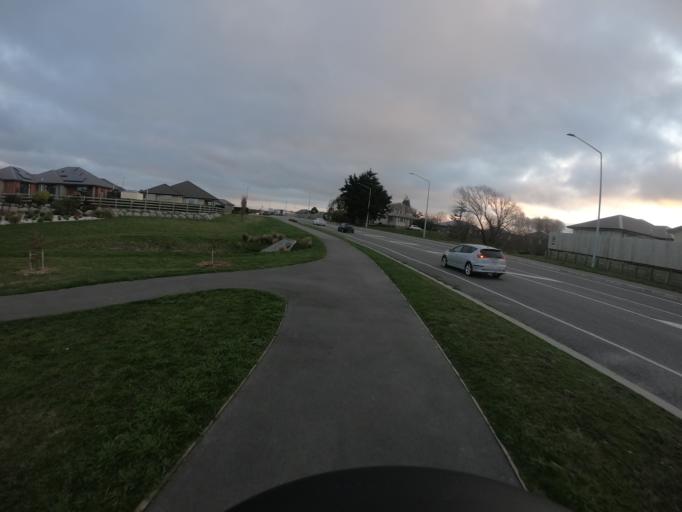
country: NZ
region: Canterbury
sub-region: Selwyn District
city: Prebbleton
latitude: -43.5596
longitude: 172.5567
